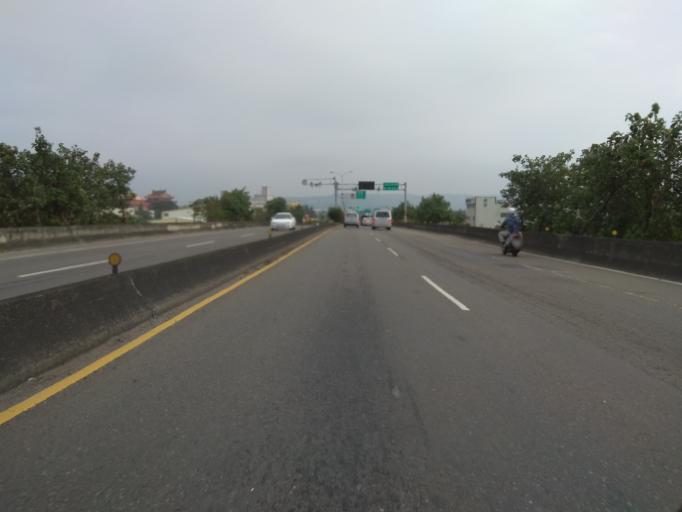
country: TW
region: Taiwan
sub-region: Hsinchu
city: Hsinchu
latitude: 24.8507
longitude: 120.9417
